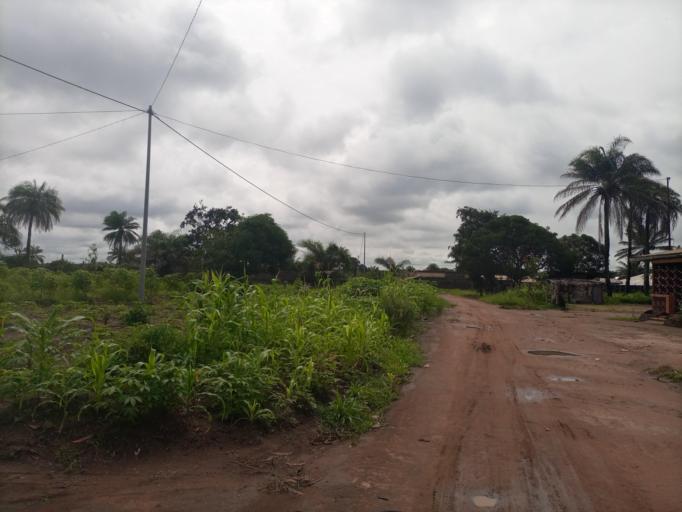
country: SL
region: Northern Province
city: Sawkta
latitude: 8.6245
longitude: -13.1987
